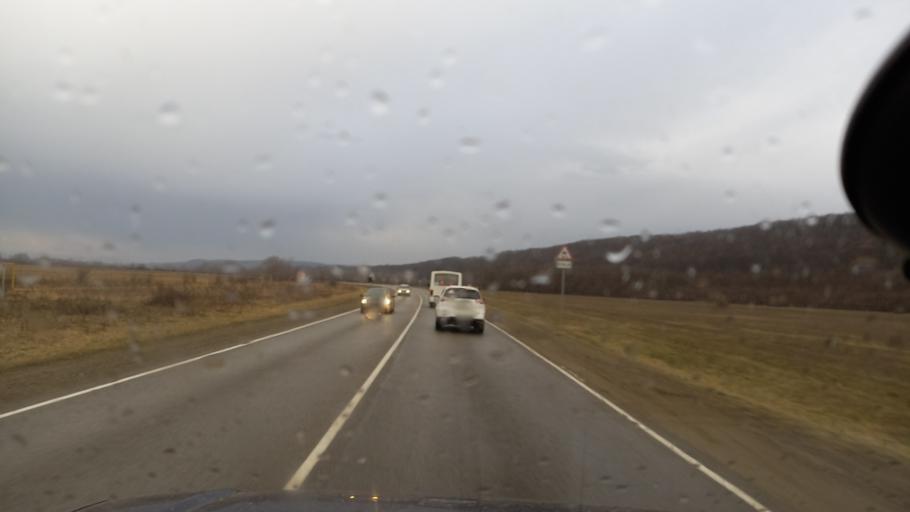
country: RU
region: Adygeya
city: Tul'skiy
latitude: 44.5253
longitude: 40.1354
